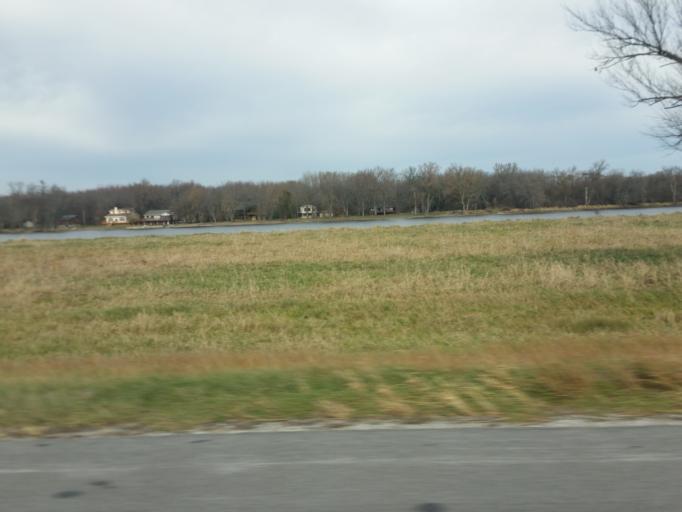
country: US
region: Illinois
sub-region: Rock Island County
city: Coal Valley
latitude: 41.4529
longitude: -90.4526
